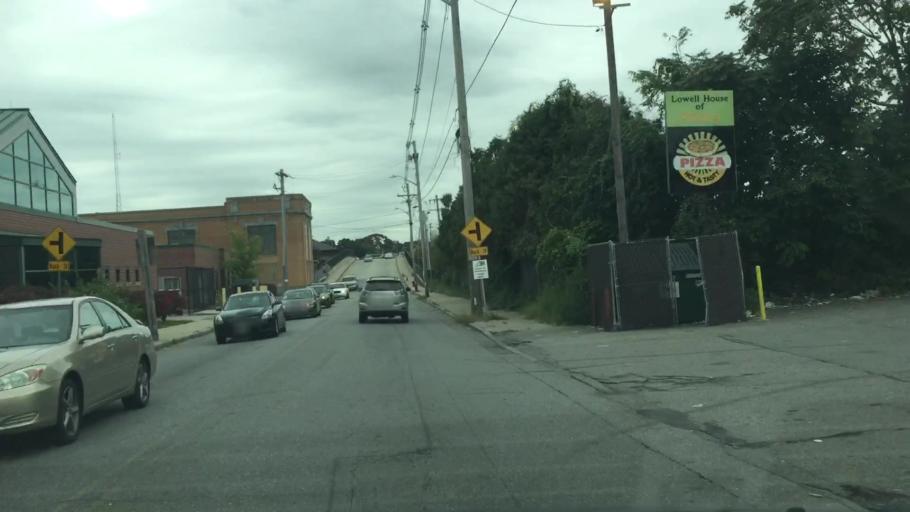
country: US
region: Massachusetts
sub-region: Middlesex County
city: Lowell
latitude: 42.6431
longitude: -71.3259
